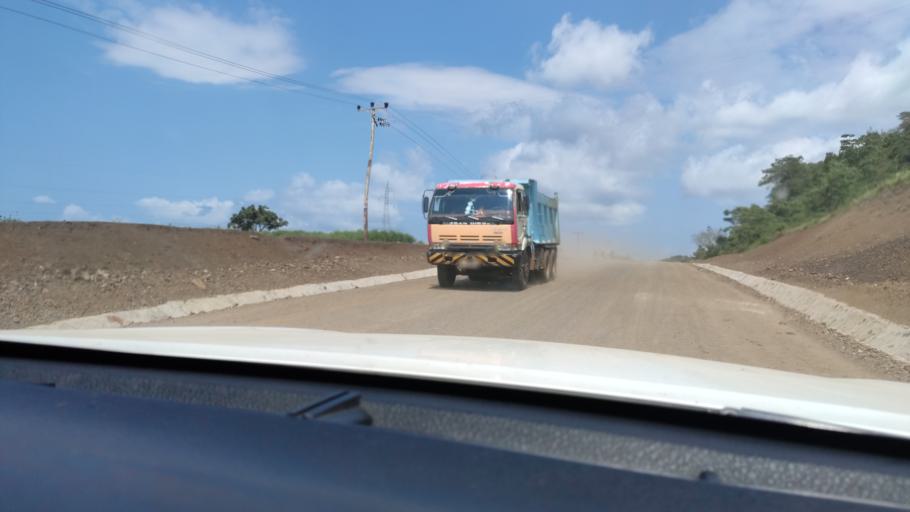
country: ET
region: Southern Nations, Nationalities, and People's Region
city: Felege Neway
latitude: 6.3944
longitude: 37.0746
